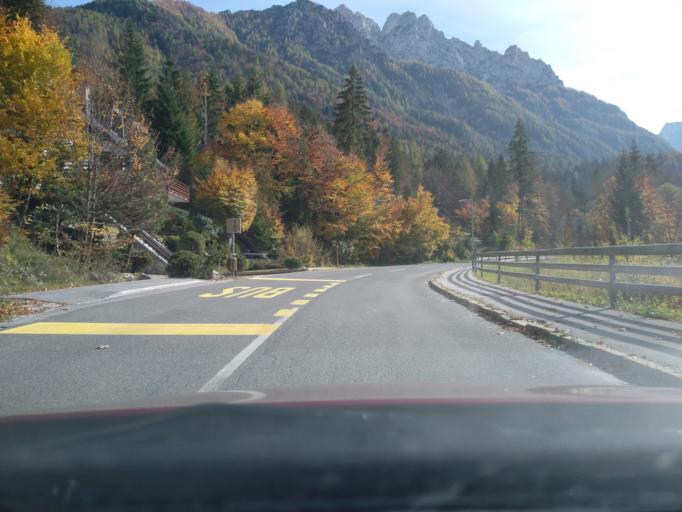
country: SI
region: Kranjska Gora
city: Kranjska Gora
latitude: 46.4750
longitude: 13.7846
